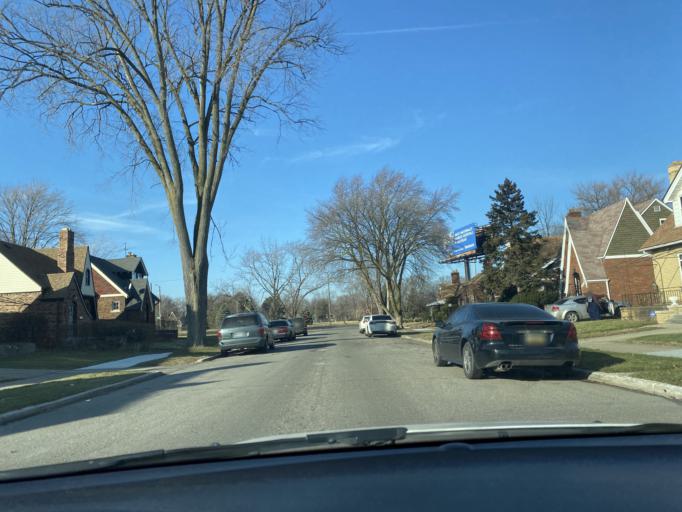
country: US
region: Michigan
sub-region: Wayne County
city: Harper Woods
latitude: 42.4085
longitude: -82.9464
